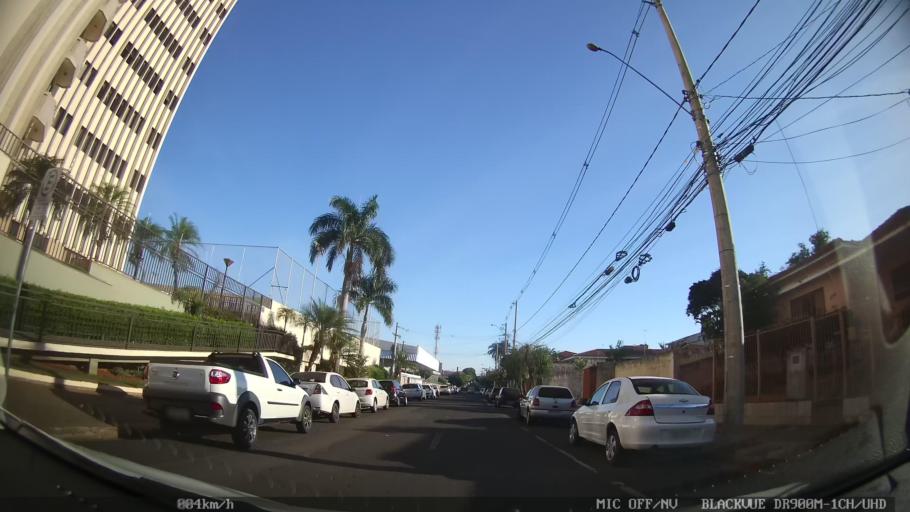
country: BR
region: Sao Paulo
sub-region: Sao Jose Do Rio Preto
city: Sao Jose do Rio Preto
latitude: -20.8195
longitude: -49.3988
